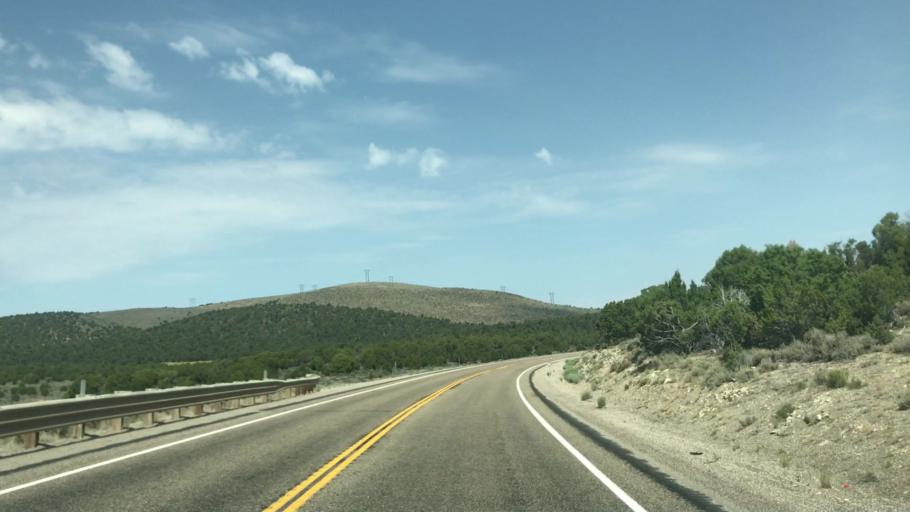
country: US
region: Nevada
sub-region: White Pine County
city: Ely
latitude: 39.3923
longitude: -115.0818
